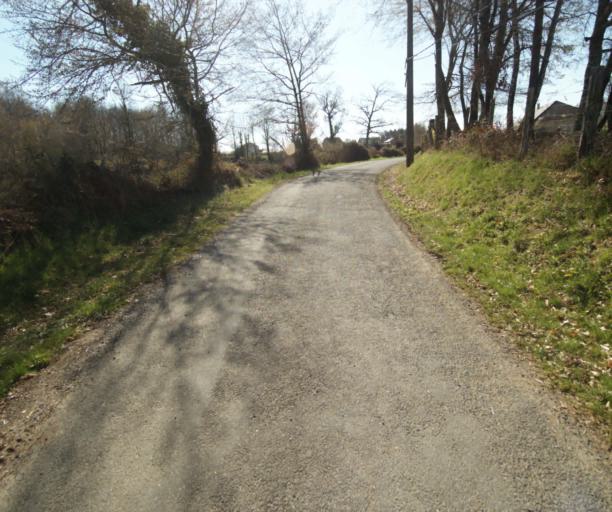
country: FR
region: Limousin
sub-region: Departement de la Correze
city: Saint-Mexant
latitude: 45.3099
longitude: 1.6011
